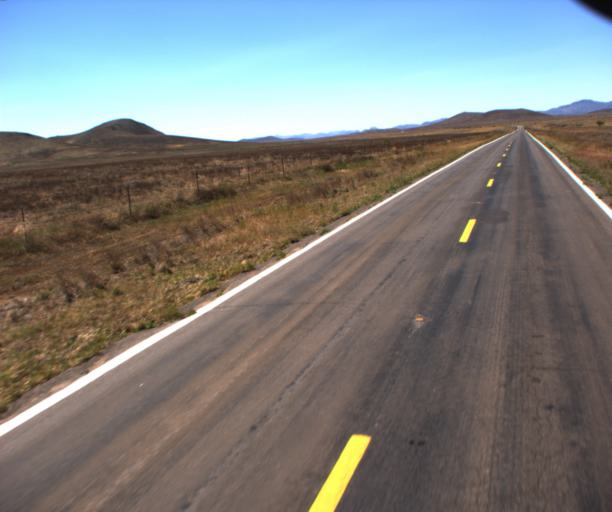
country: US
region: Arizona
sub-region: Cochise County
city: Douglas
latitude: 31.5879
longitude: -109.2461
